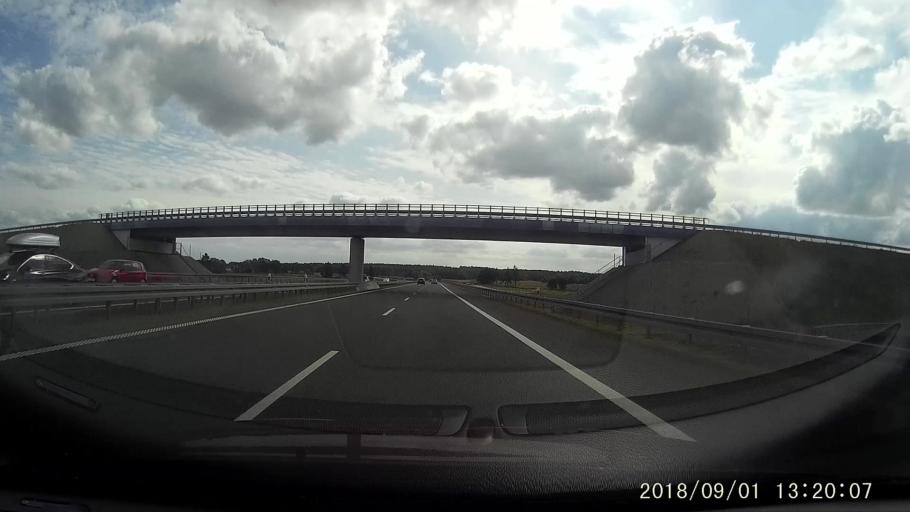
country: PL
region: West Pomeranian Voivodeship
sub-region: Powiat pyrzycki
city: Bielice
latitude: 53.1800
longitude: 14.6915
